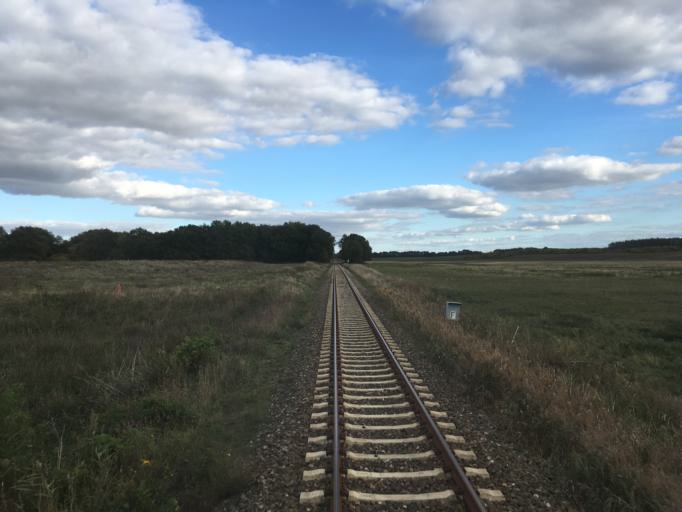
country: DE
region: Mecklenburg-Vorpommern
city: Grabowhofe
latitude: 53.5423
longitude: 12.5849
